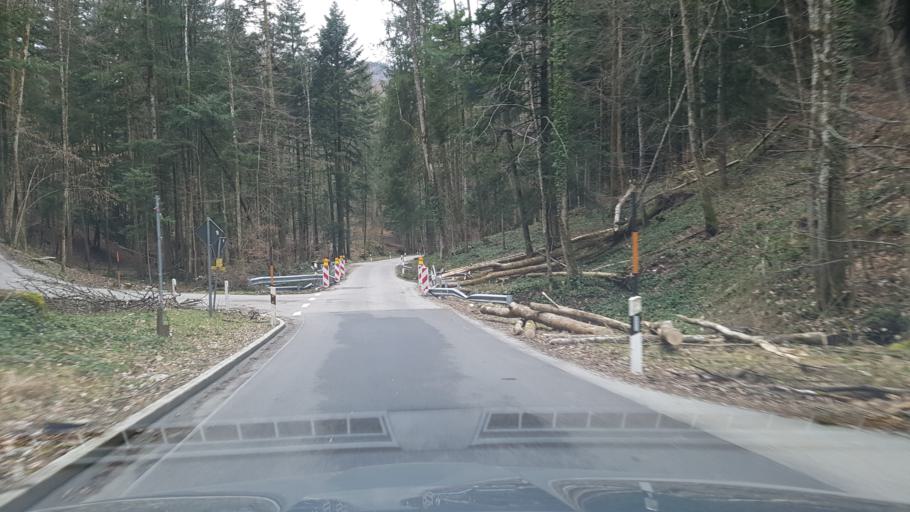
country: DE
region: Bavaria
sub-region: Upper Bavaria
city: Marktschellenberg
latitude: 47.6851
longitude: 13.0602
